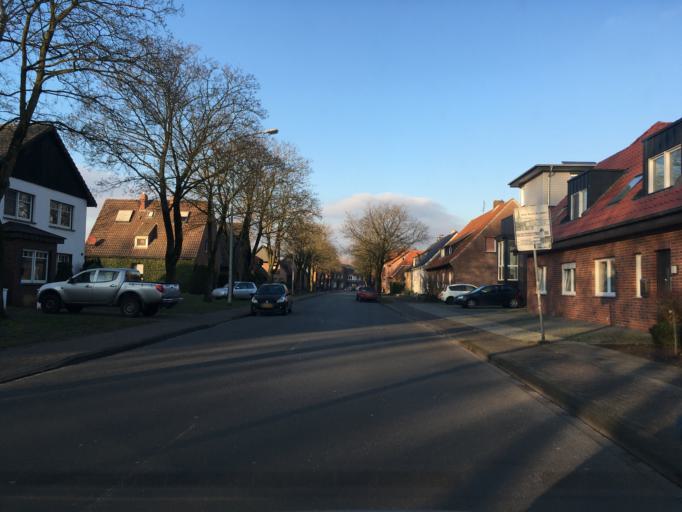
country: DE
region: North Rhine-Westphalia
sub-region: Regierungsbezirk Munster
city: Gronau
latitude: 52.1721
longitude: 7.0347
